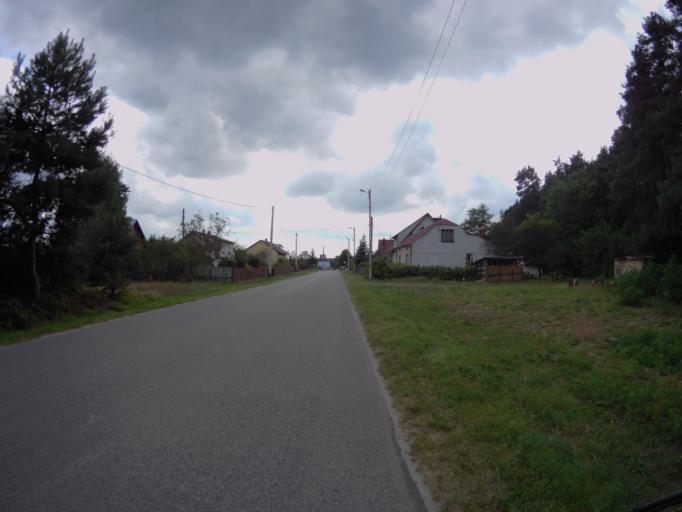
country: PL
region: Subcarpathian Voivodeship
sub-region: Powiat lezajski
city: Brzoza Krolewska
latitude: 50.2413
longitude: 22.3223
